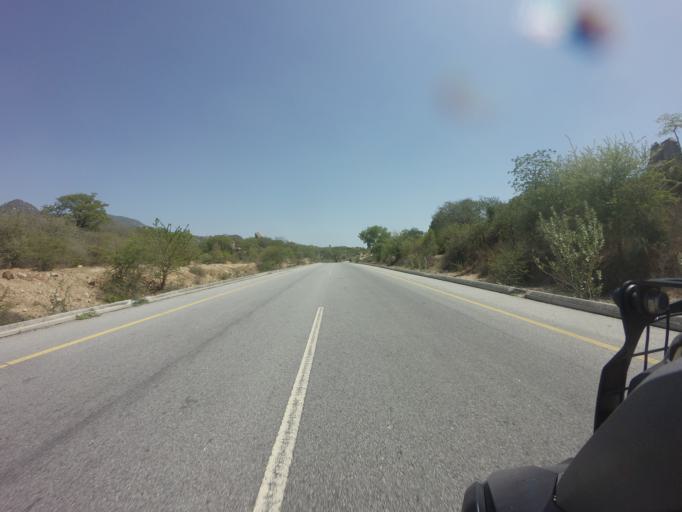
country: AO
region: Benguela
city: Benguela
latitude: -13.1563
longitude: 13.7673
